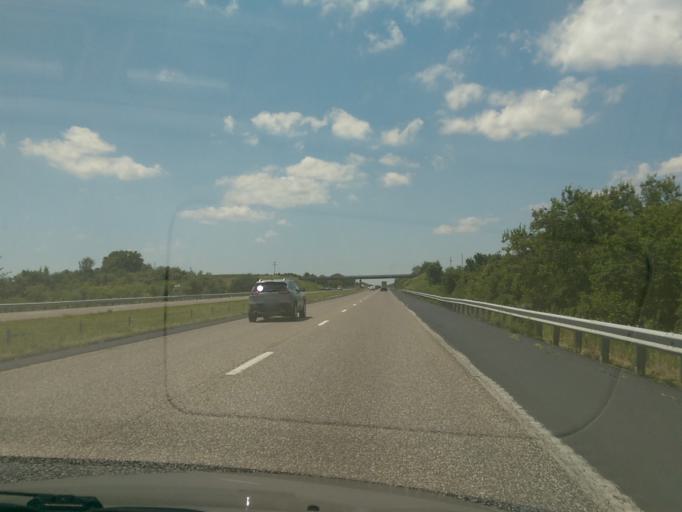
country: US
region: Missouri
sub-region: Cooper County
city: Boonville
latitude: 38.9392
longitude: -92.6252
